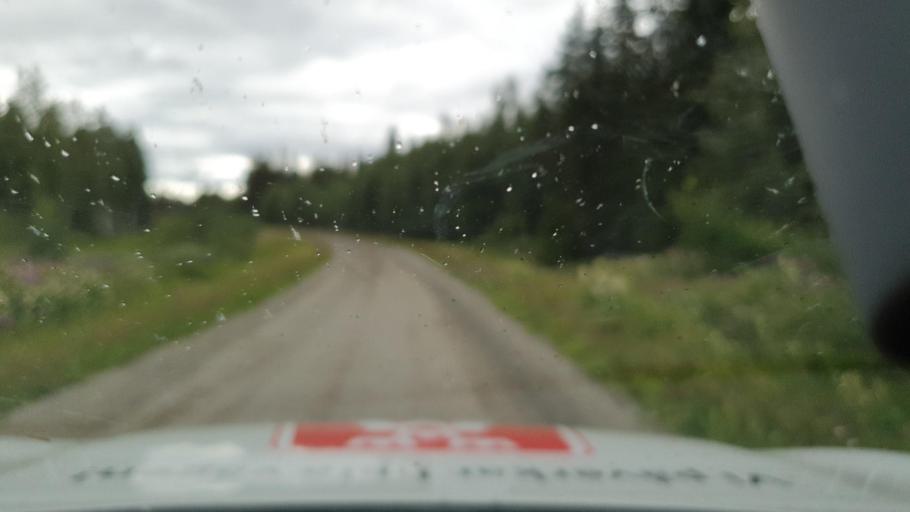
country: SE
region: Vaesterbotten
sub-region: Dorotea Kommun
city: Dorotea
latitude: 64.1960
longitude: 16.6806
